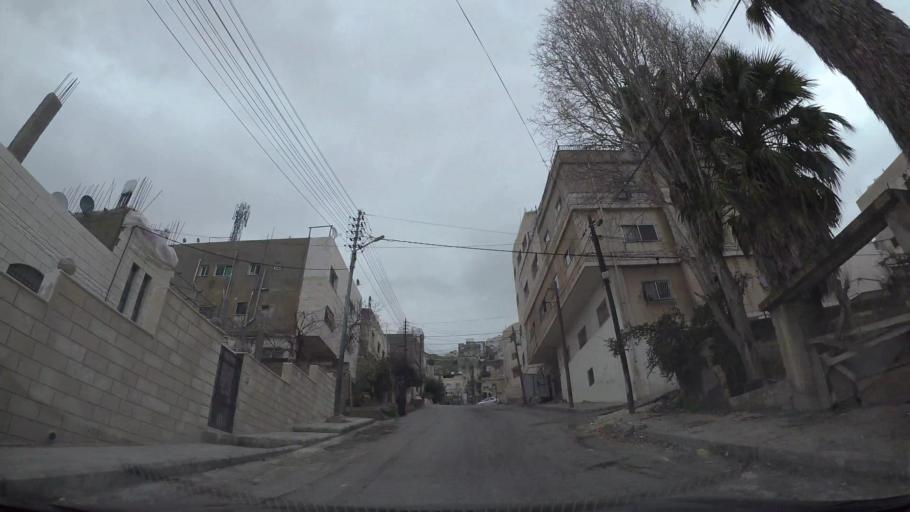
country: JO
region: Amman
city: Wadi as Sir
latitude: 31.9513
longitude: 35.8227
